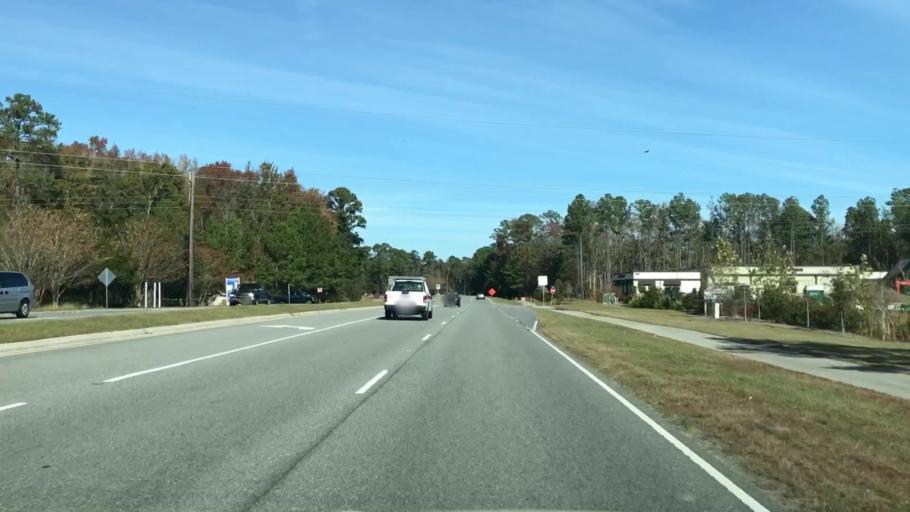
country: US
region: South Carolina
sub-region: Beaufort County
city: Bluffton
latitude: 32.2844
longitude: -80.9100
